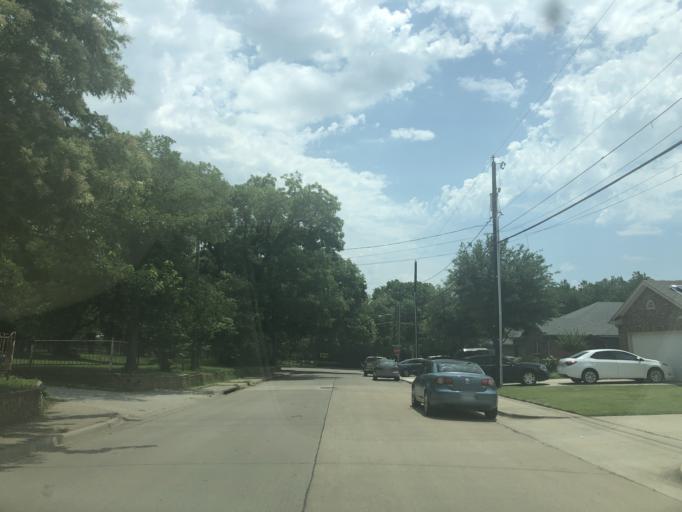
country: US
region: Texas
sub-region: Dallas County
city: Irving
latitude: 32.7939
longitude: -96.9310
